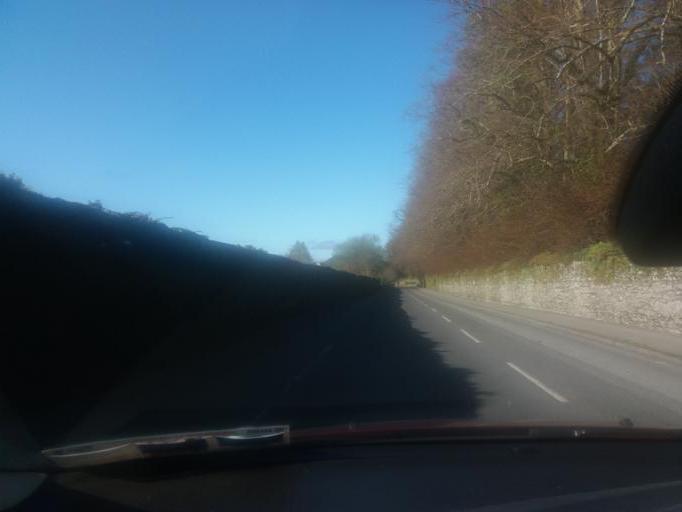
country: IE
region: Munster
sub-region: Ciarrai
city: Cill Airne
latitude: 52.0491
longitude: -9.5187
